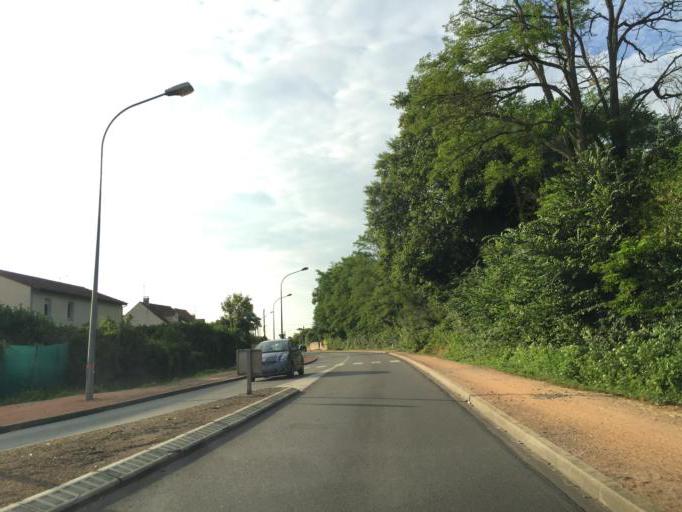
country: FR
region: Auvergne
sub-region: Departement de l'Allier
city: Creuzier-le-Vieux
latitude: 46.1511
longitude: 3.4134
